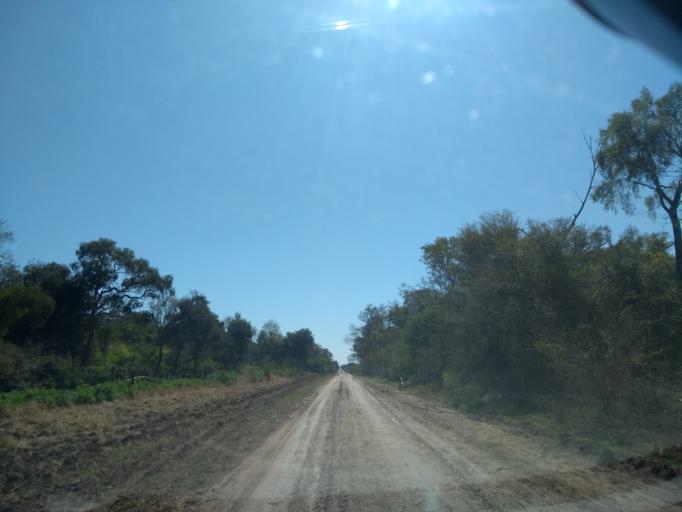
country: AR
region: Chaco
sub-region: Departamento de Quitilipi
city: Quitilipi
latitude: -26.7164
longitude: -60.2254
